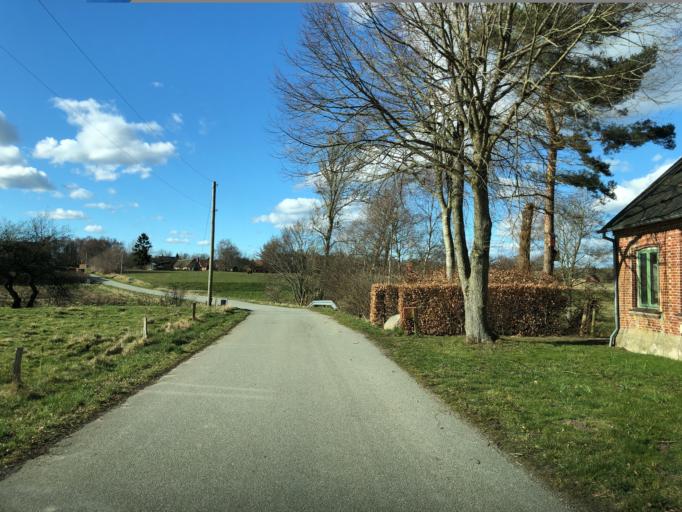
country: DK
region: Central Jutland
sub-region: Randers Kommune
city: Langa
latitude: 56.3250
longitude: 9.9133
